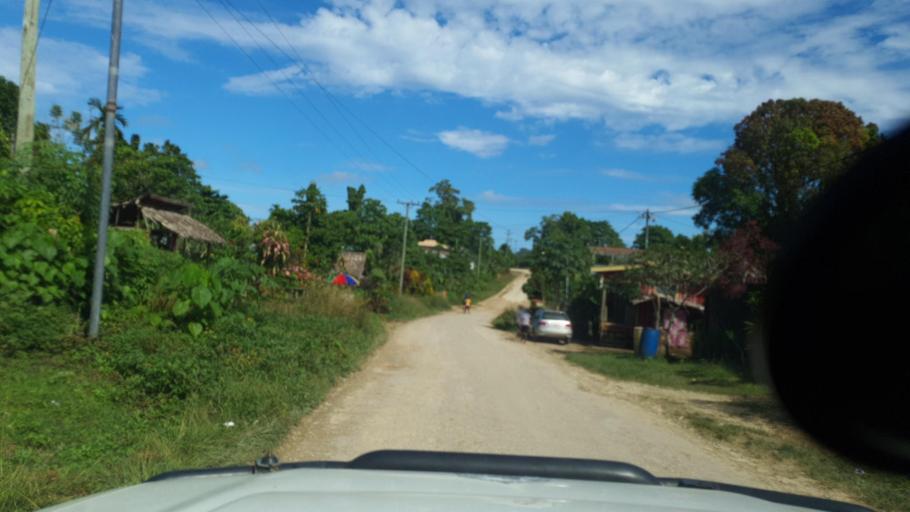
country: SB
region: Western Province
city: Gizo
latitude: -8.2437
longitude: 157.1982
